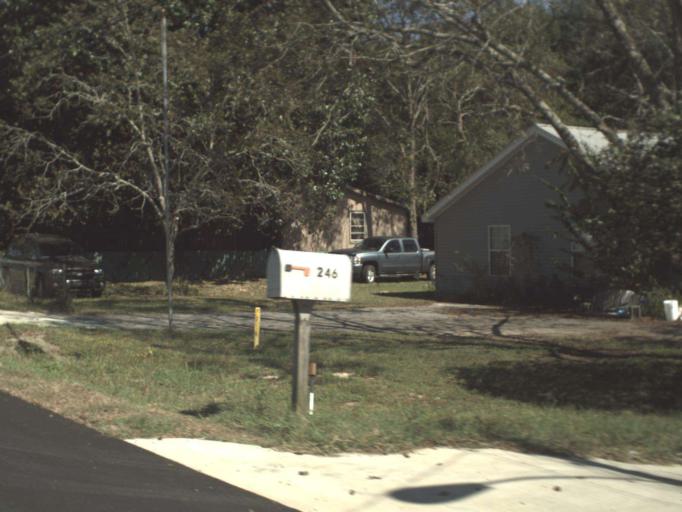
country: US
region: Florida
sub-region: Walton County
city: DeFuniak Springs
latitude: 30.7377
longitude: -86.1484
